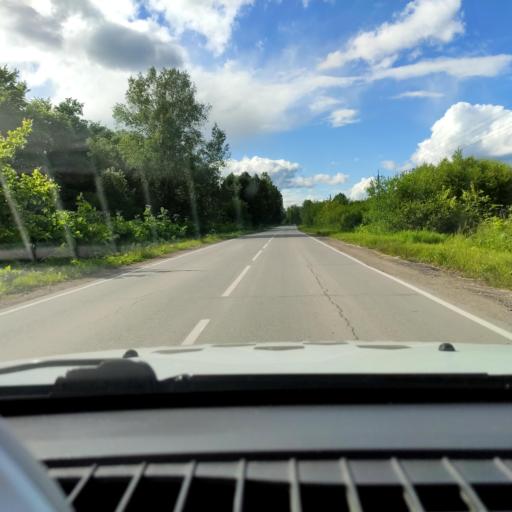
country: RU
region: Perm
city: Overyata
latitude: 58.1001
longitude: 55.8544
